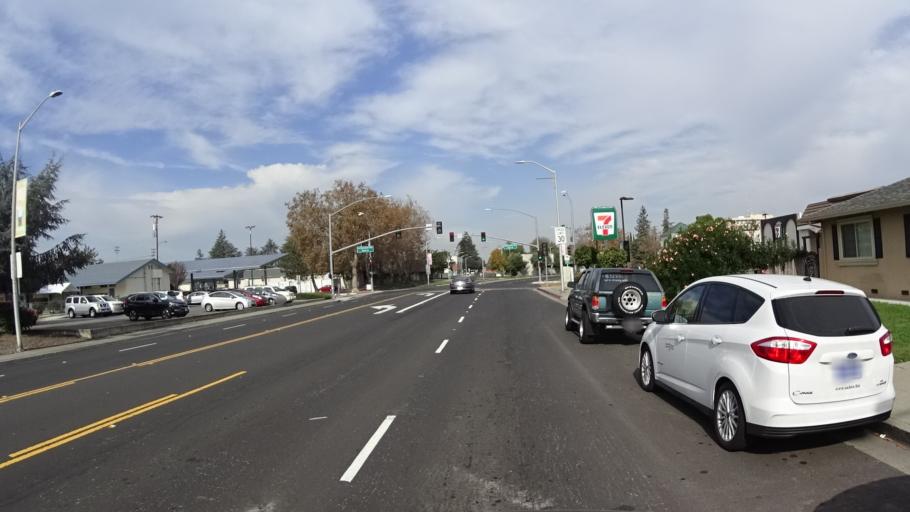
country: US
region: California
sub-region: Santa Clara County
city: Santa Clara
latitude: 37.3429
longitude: -121.9406
